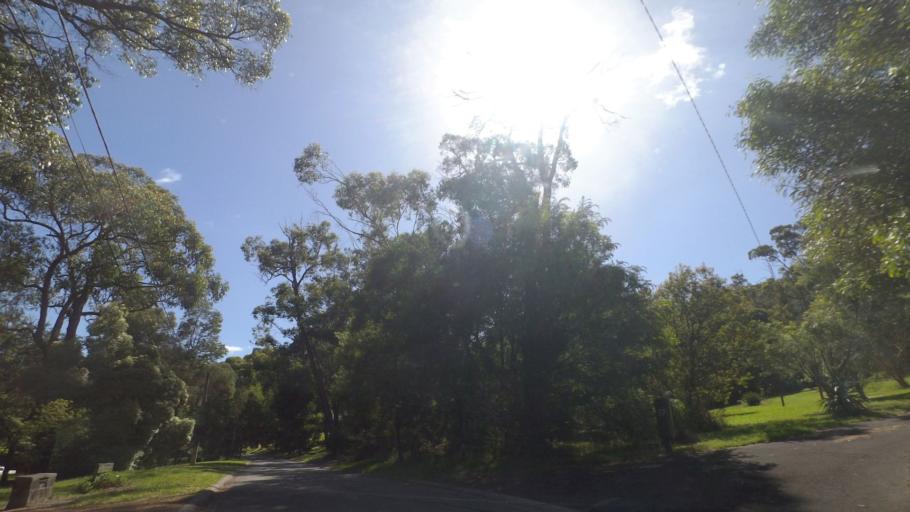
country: AU
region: Victoria
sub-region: Yarra Ranges
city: Kalorama
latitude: -37.8029
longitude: 145.3775
